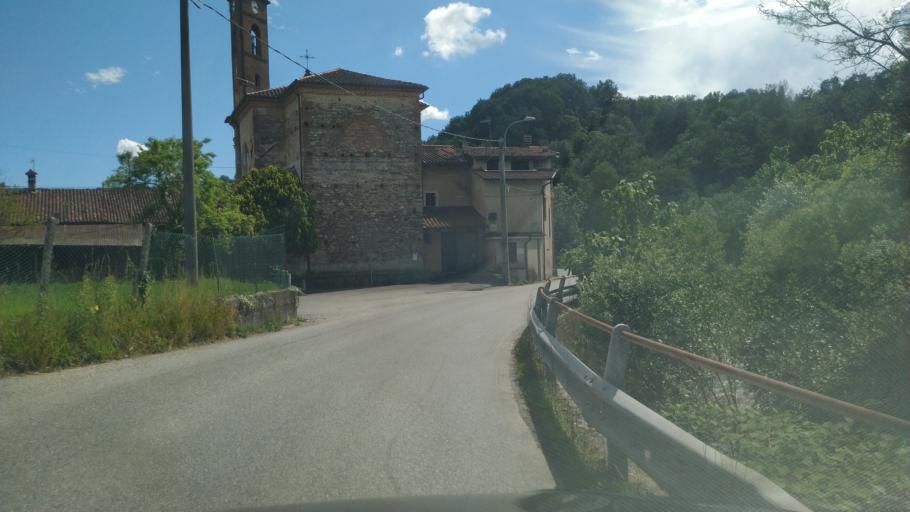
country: IT
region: Piedmont
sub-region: Provincia di Torino
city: Castellamonte
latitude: 45.3937
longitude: 7.7234
